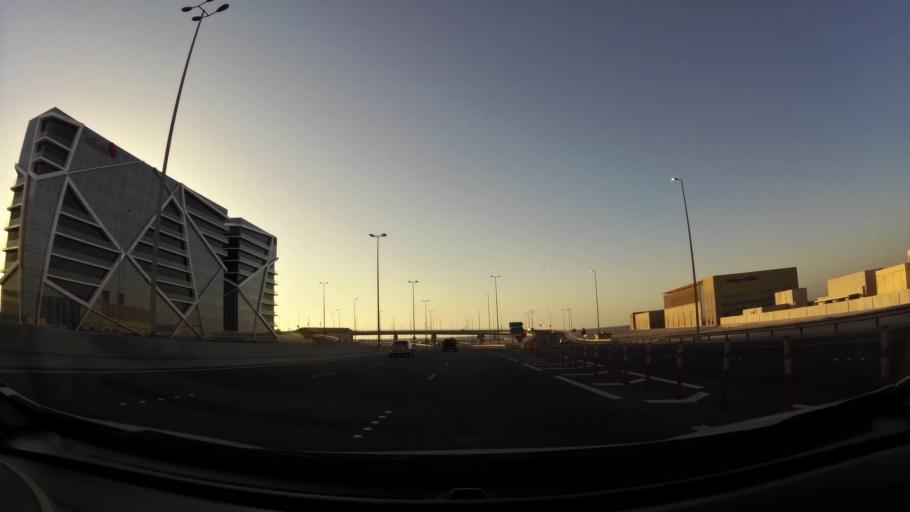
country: BH
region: Muharraq
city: Al Muharraq
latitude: 26.2512
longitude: 50.5843
